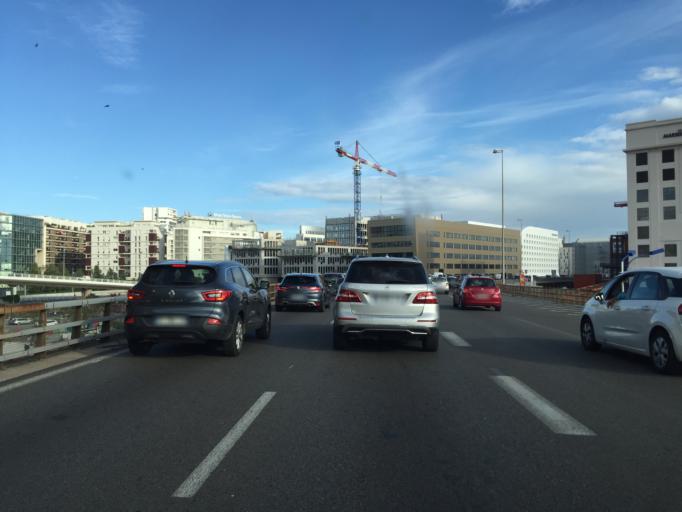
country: FR
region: Provence-Alpes-Cote d'Azur
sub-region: Departement des Bouches-du-Rhone
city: Marseille 03
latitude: 43.3125
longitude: 5.3667
